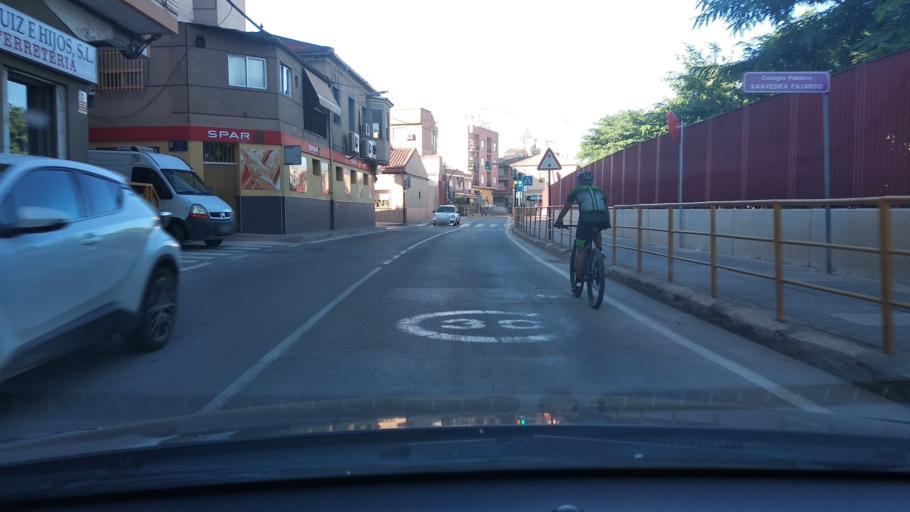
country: ES
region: Murcia
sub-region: Murcia
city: Murcia
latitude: 37.9458
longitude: -1.1085
